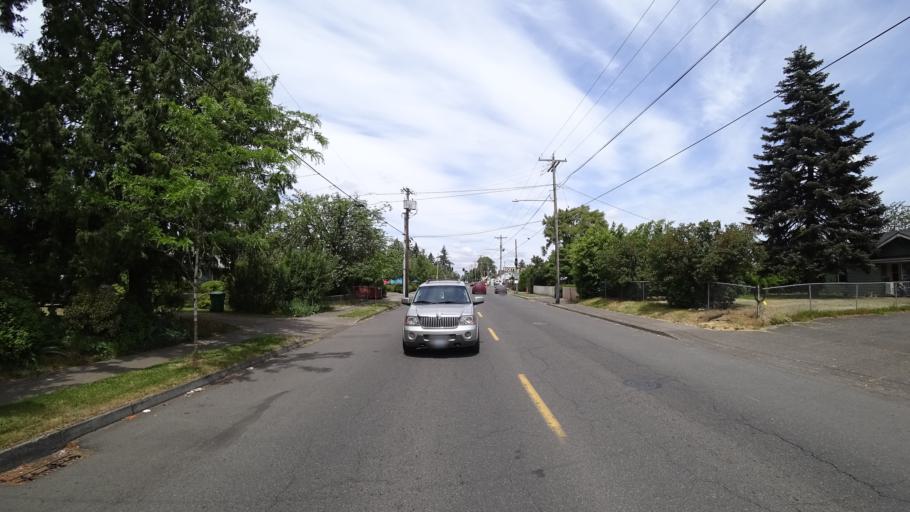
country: US
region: Oregon
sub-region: Multnomah County
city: Lents
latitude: 45.4675
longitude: -122.5894
